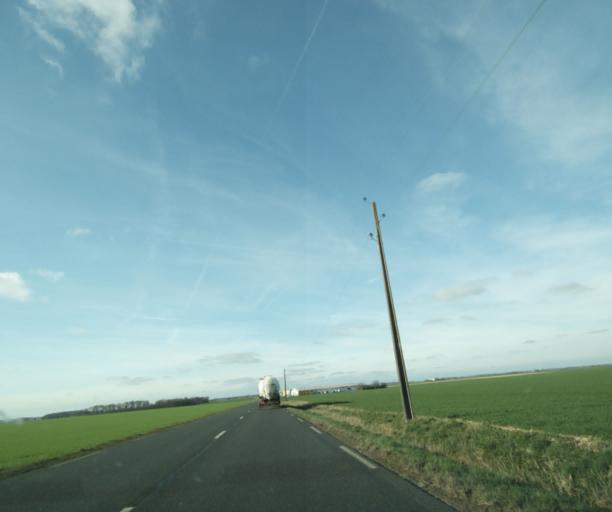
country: FR
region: Ile-de-France
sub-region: Departement des Yvelines
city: Ablis
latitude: 48.4887
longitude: 1.8465
